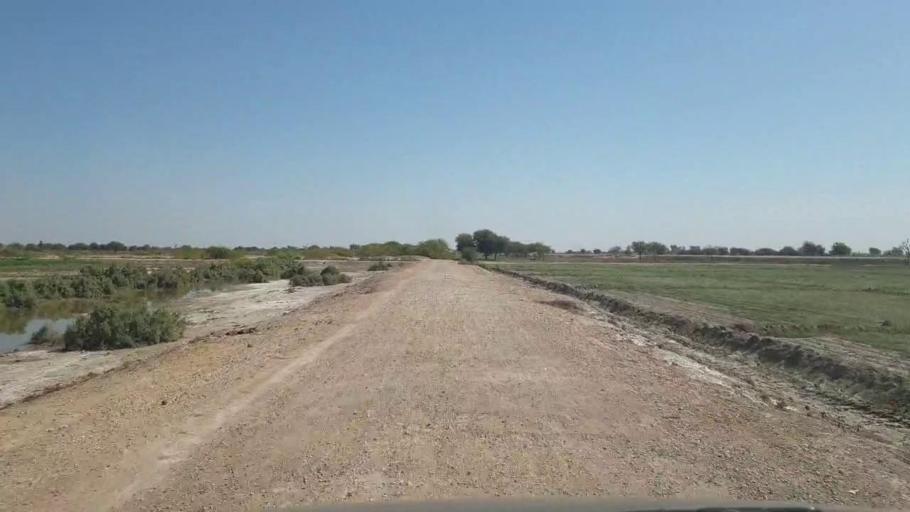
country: PK
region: Sindh
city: Dhoro Naro
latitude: 25.4578
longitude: 69.6111
